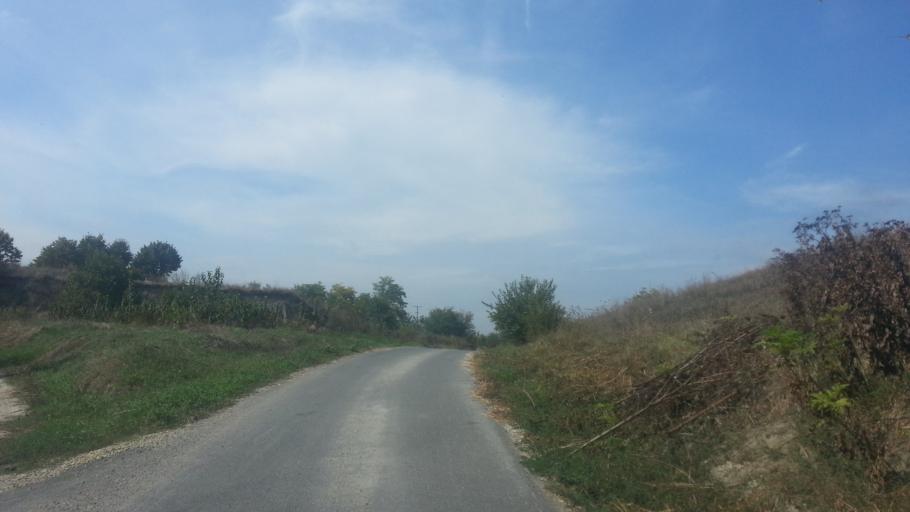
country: RS
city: Stari Banovci
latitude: 44.9874
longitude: 20.2772
